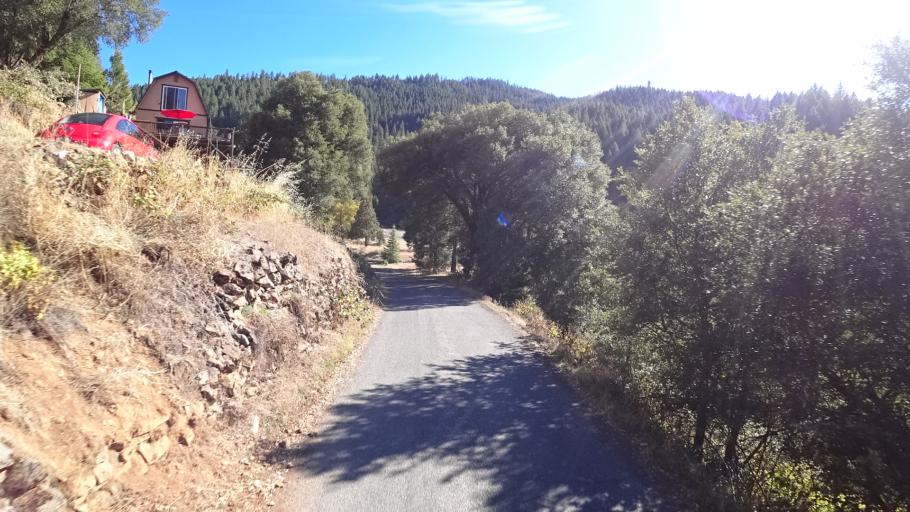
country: US
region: California
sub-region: Siskiyou County
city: Happy Camp
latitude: 41.2978
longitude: -123.1317
